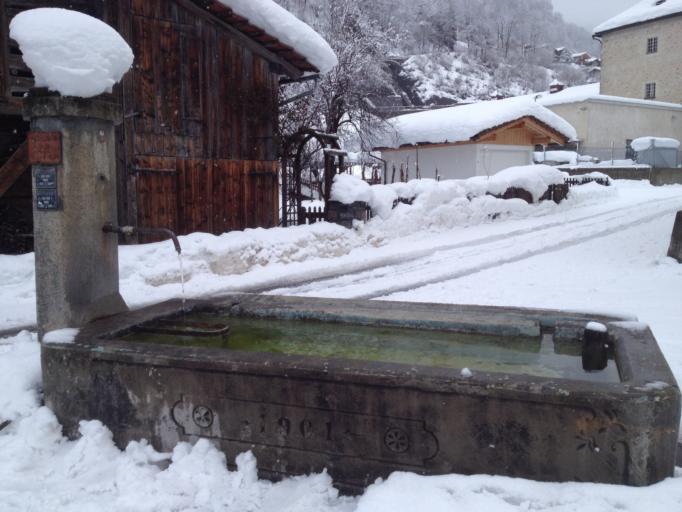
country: CH
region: Grisons
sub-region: Praettigau/Davos District
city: Luzein
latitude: 46.9136
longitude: 9.7803
